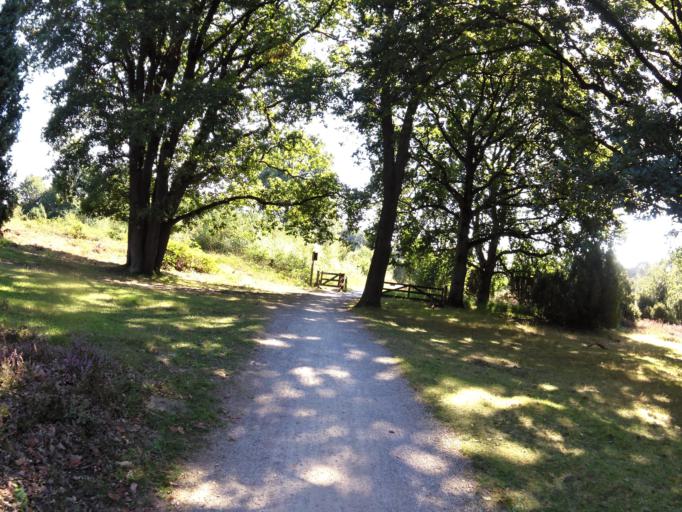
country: NL
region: Overijssel
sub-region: Gemeente Haaksbergen
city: Haaksbergen
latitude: 52.1555
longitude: 6.7987
